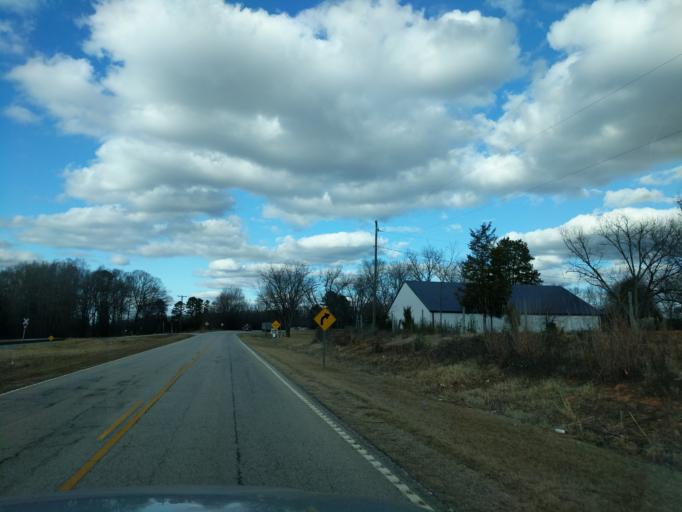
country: US
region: South Carolina
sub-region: Laurens County
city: Watts Mills
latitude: 34.5920
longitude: -81.9946
